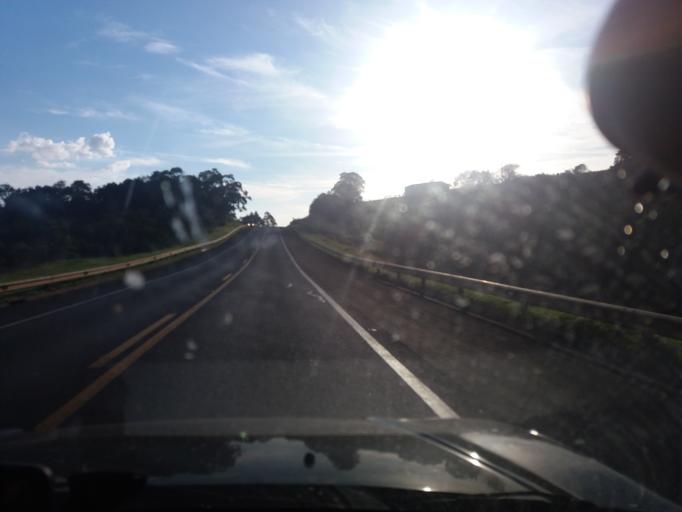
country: BR
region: Sao Paulo
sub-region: Buri
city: Buri
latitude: -23.9352
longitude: -48.6292
